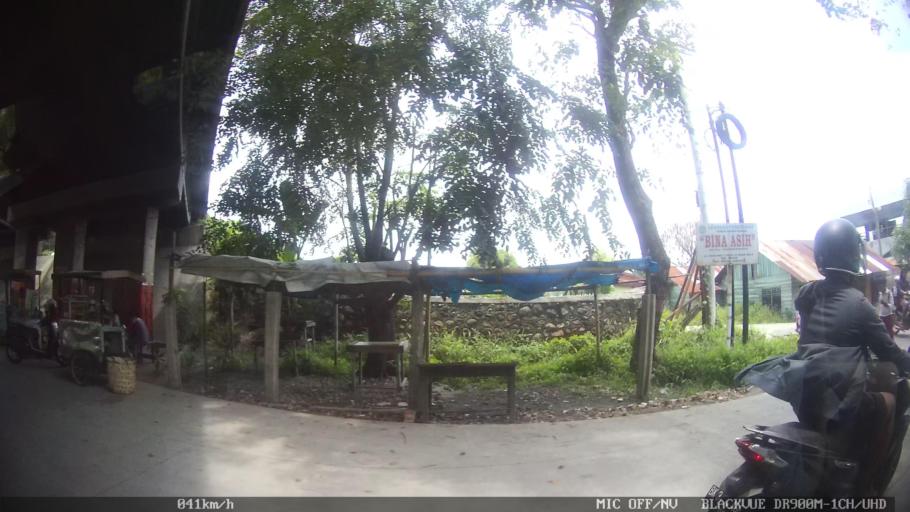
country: ID
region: North Sumatra
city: Labuhan Deli
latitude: 3.6915
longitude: 98.6818
